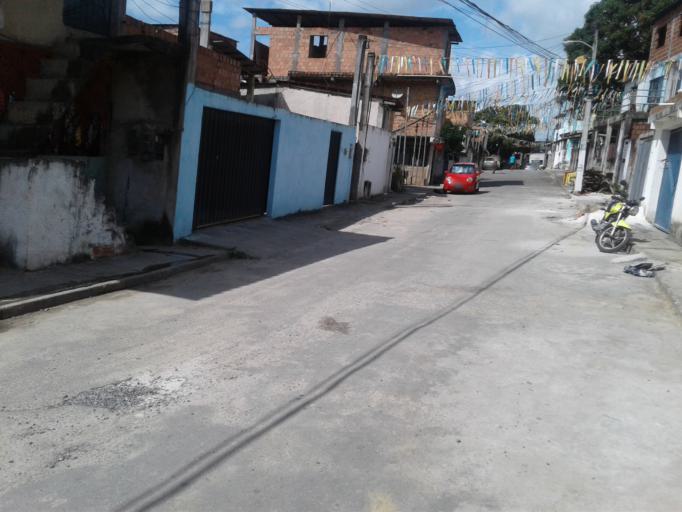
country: BR
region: Bahia
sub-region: Salvador
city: Salvador
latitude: -12.8808
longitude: -38.4741
